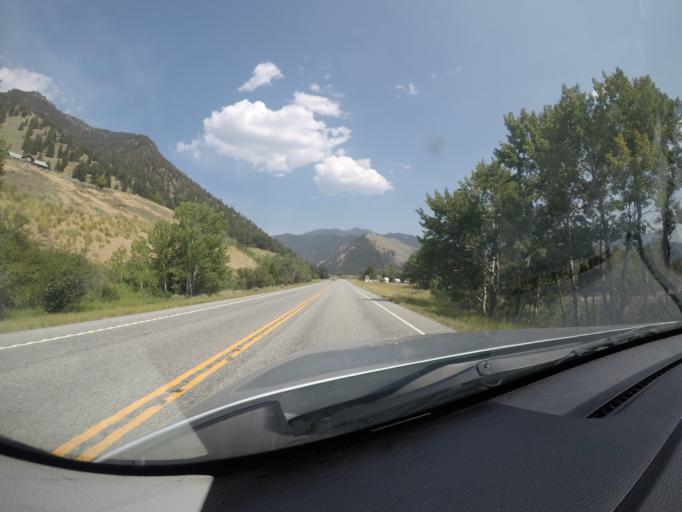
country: US
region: Montana
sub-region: Gallatin County
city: West Yellowstone
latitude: 44.8272
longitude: -111.4606
